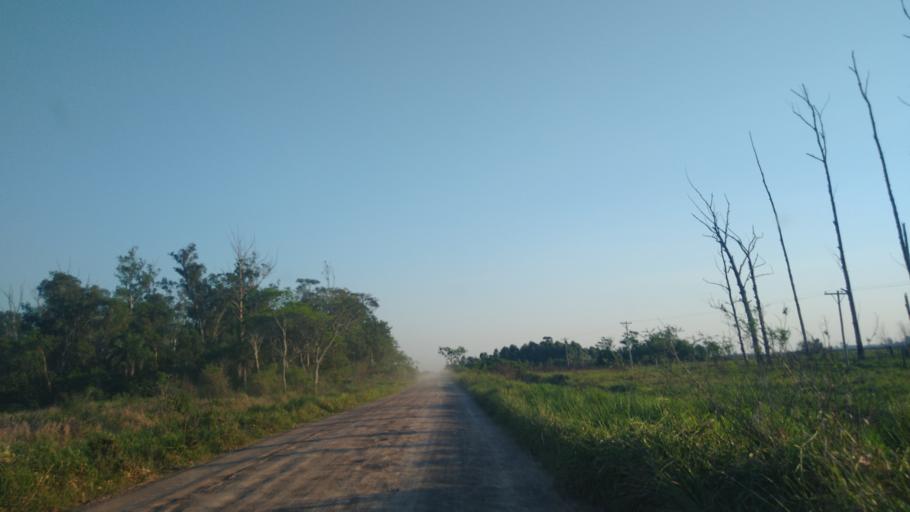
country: PY
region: Neembucu
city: Cerrito
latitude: -27.3988
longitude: -57.6587
